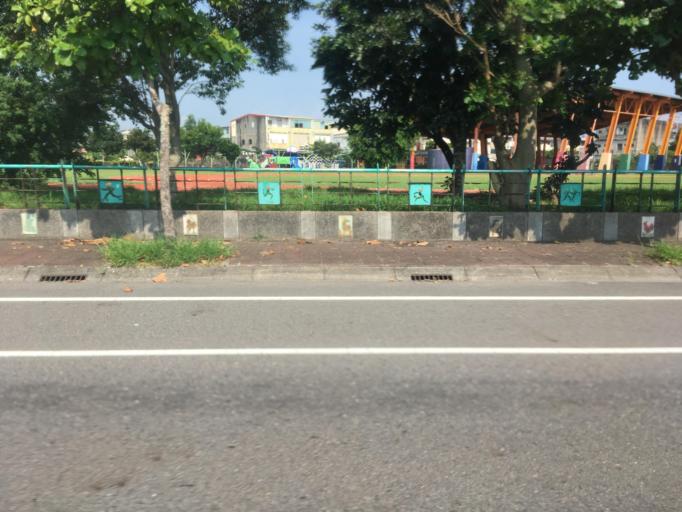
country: TW
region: Taiwan
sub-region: Yilan
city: Yilan
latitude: 24.6406
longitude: 121.8343
